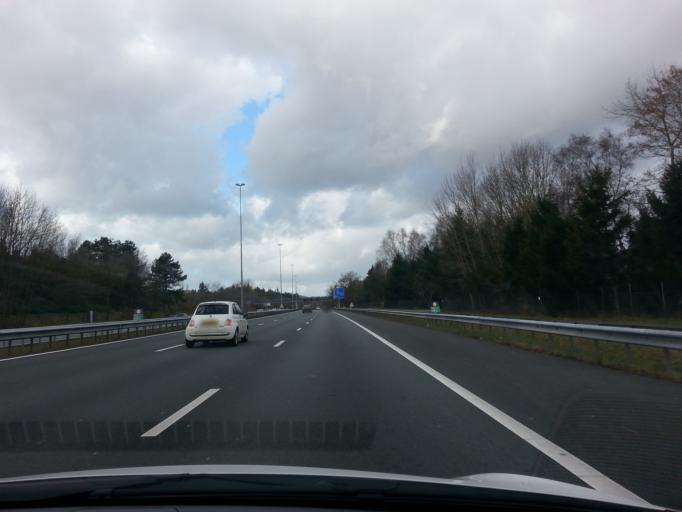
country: NL
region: North Brabant
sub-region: Gemeente Boxtel
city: Boxtel
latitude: 51.6067
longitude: 5.3287
